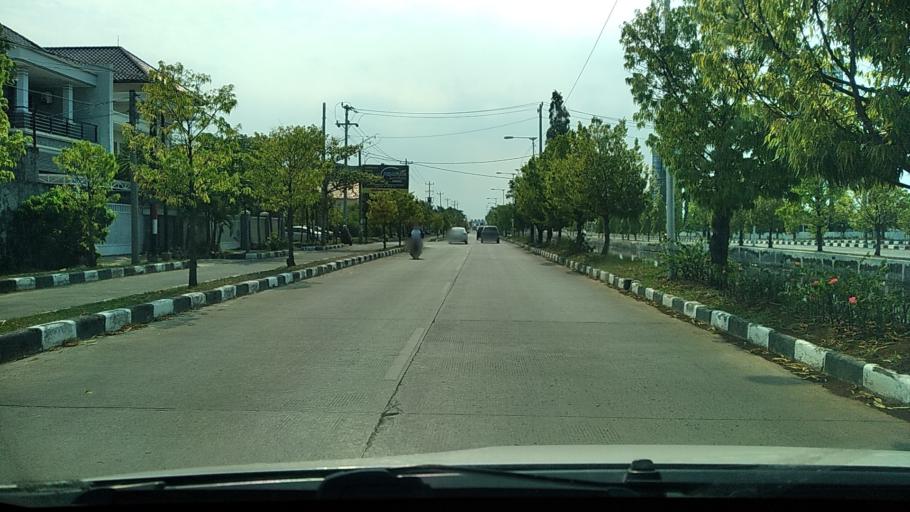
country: ID
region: Central Java
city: Semarang
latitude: -6.9630
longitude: 110.3870
